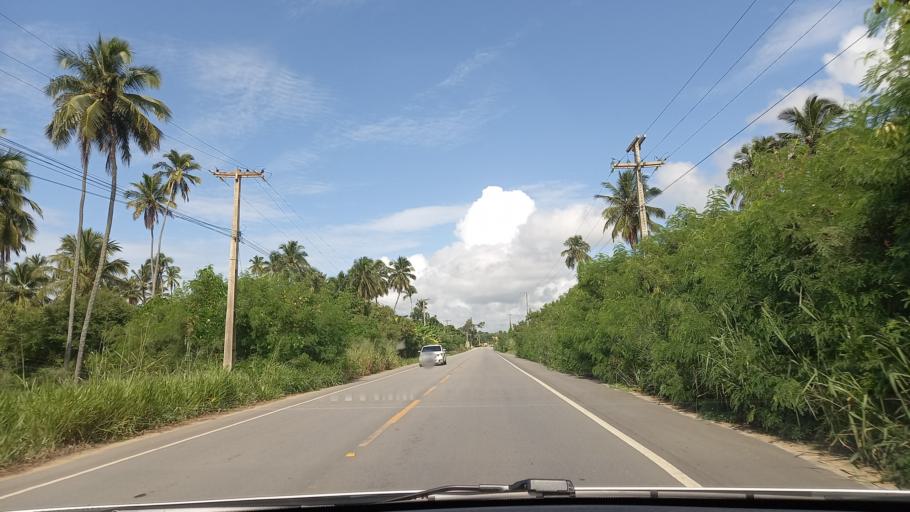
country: BR
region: Alagoas
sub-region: Maragogi
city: Maragogi
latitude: -8.9795
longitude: -35.1871
